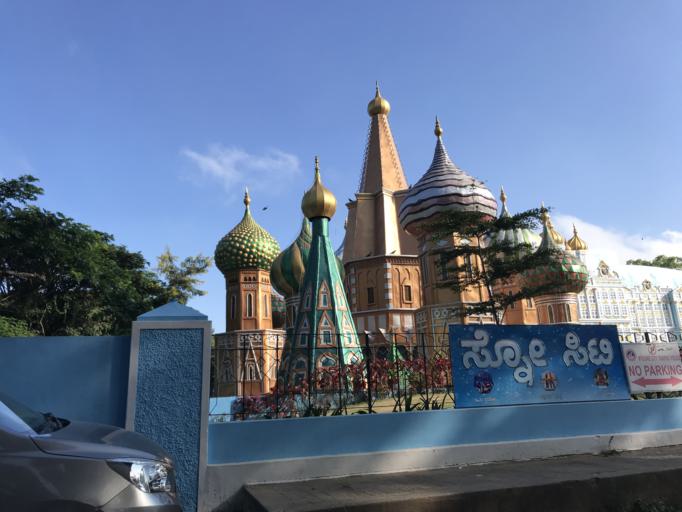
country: IN
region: Karnataka
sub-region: Mysore
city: Mysore
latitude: 12.3050
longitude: 76.6653
